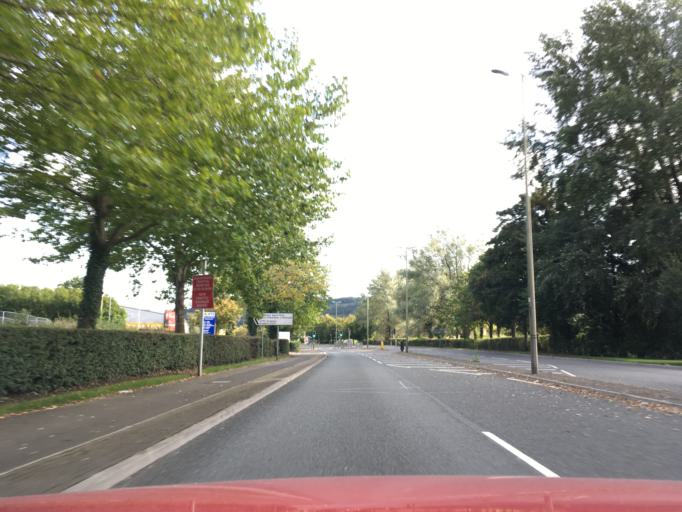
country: GB
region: Wales
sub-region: Caerphilly County Borough
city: Abertridwr
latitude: 51.5714
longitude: -3.2878
